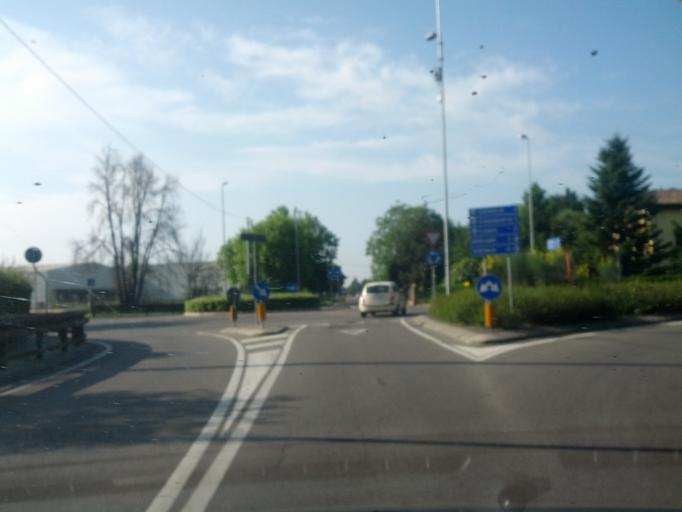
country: IT
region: Emilia-Romagna
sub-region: Provincia di Reggio Emilia
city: Campagnola Emilia
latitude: 44.8374
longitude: 10.7586
